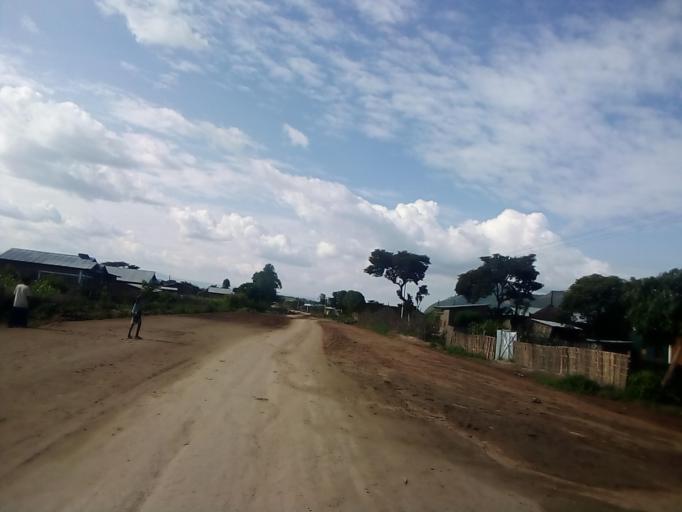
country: ET
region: Southern Nations, Nationalities, and People's Region
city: K'olito
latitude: 7.6063
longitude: 38.0662
